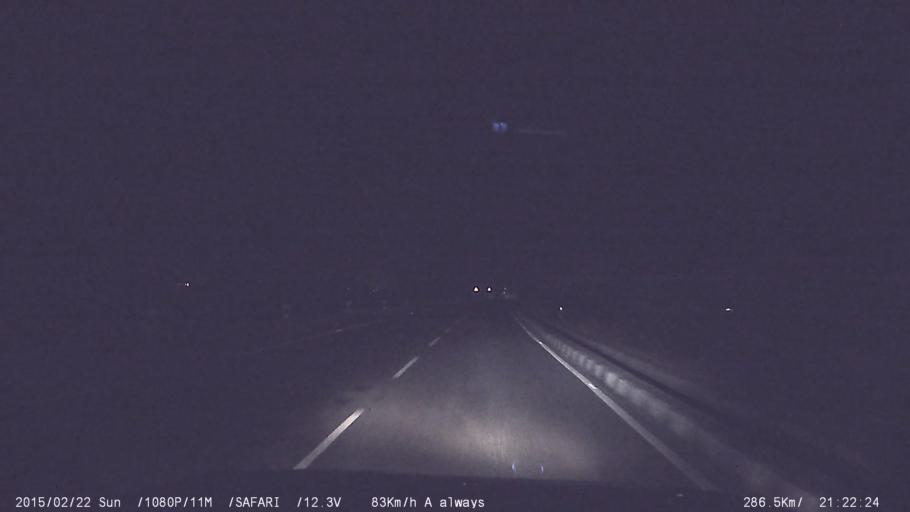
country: IN
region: Tamil Nadu
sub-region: Karur
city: Karur
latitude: 10.8732
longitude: 77.9997
